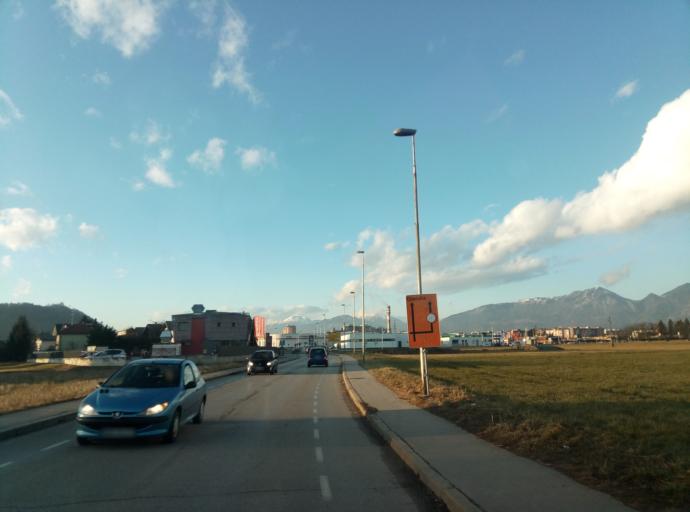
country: SI
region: Kranj
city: Kranj
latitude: 46.2283
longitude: 14.3704
